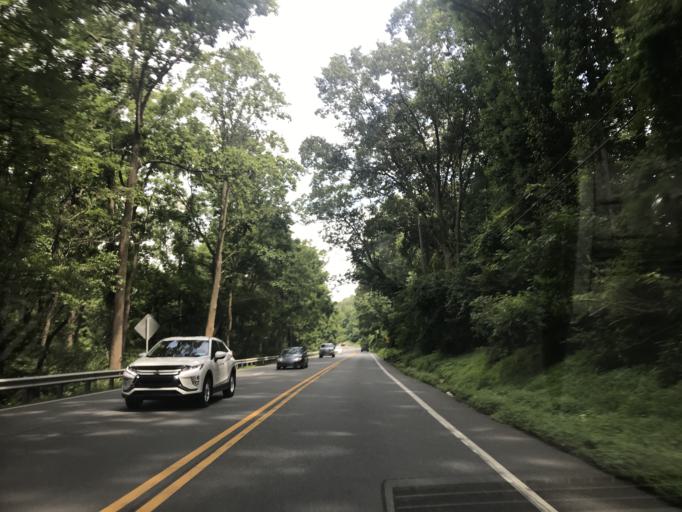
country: US
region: Delaware
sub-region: New Castle County
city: Greenville
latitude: 39.7637
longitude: -75.6450
